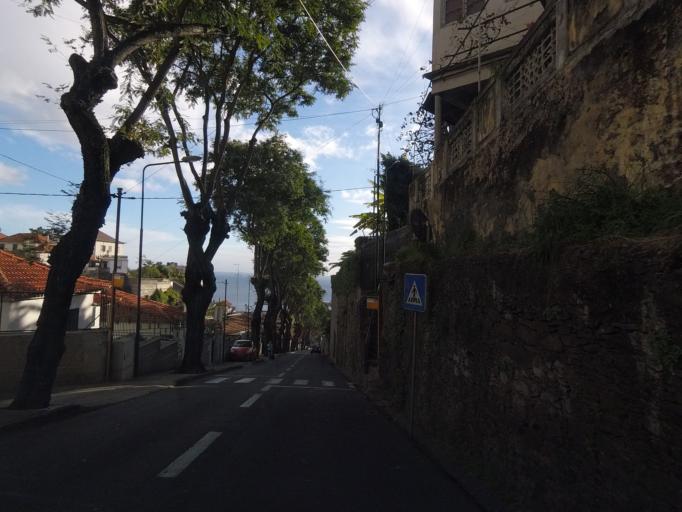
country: PT
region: Madeira
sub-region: Funchal
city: Nossa Senhora do Monte
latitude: 32.6598
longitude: -16.9027
